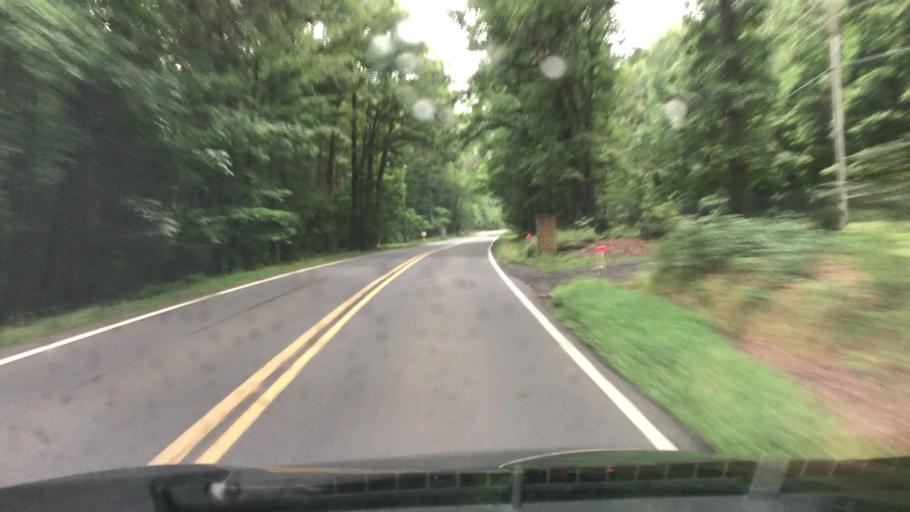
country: US
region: Virginia
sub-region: Prince William County
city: Nokesville
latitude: 38.5680
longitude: -77.6183
